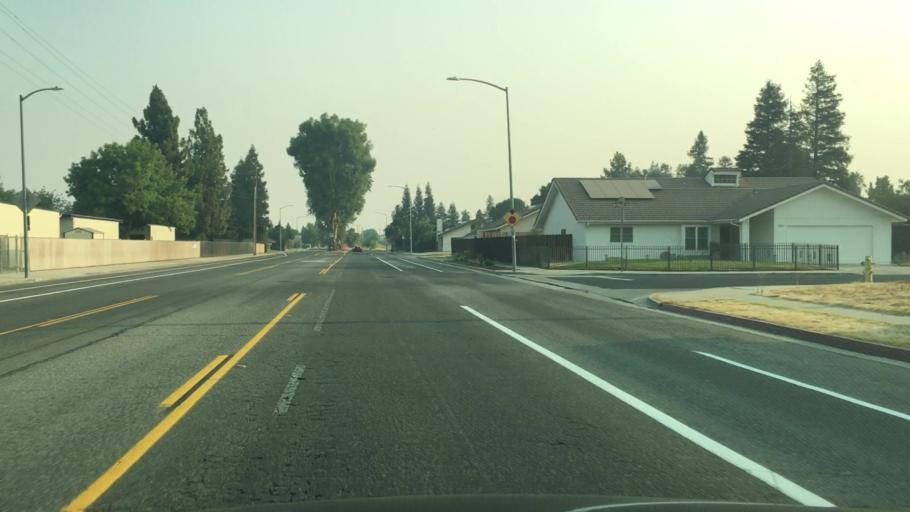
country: US
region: California
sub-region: Fresno County
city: Clovis
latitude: 36.8316
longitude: -119.6729
